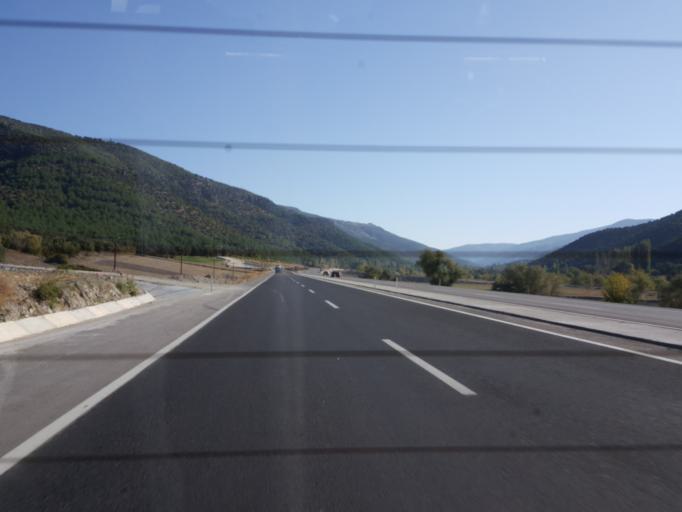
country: TR
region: Tokat
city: Turhal
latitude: 40.4677
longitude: 36.1234
